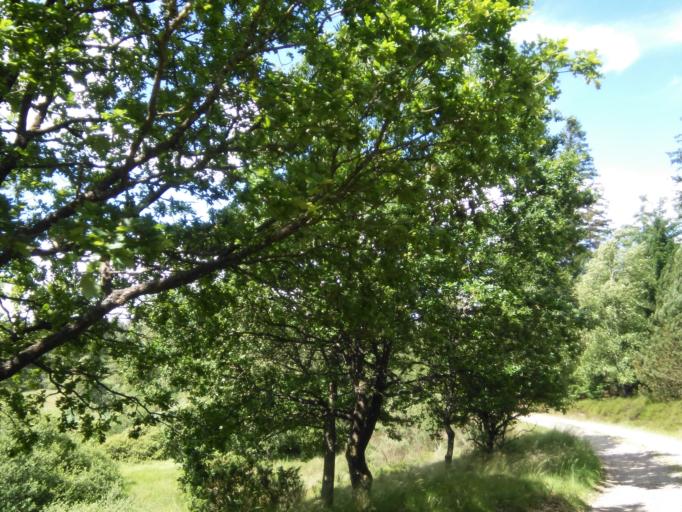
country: DK
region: Central Jutland
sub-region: Silkeborg Kommune
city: Virklund
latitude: 56.0657
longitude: 9.4515
